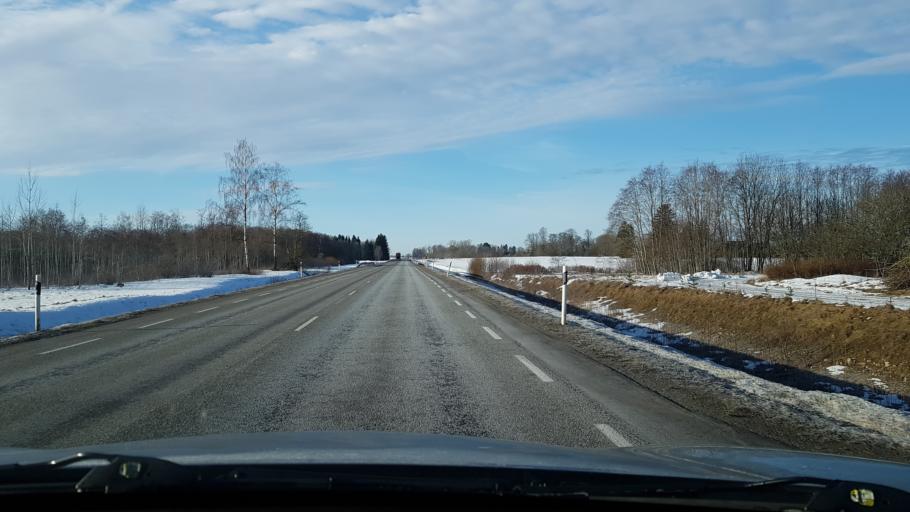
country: EE
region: Viljandimaa
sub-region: Vohma linn
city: Vohma
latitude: 58.6631
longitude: 25.6226
